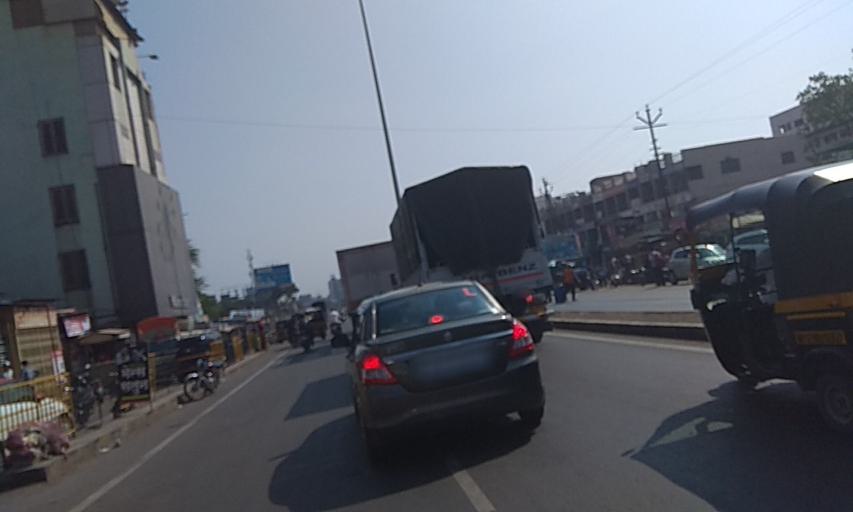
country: IN
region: Maharashtra
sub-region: Pune Division
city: Lohogaon
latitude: 18.4893
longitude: 74.0213
